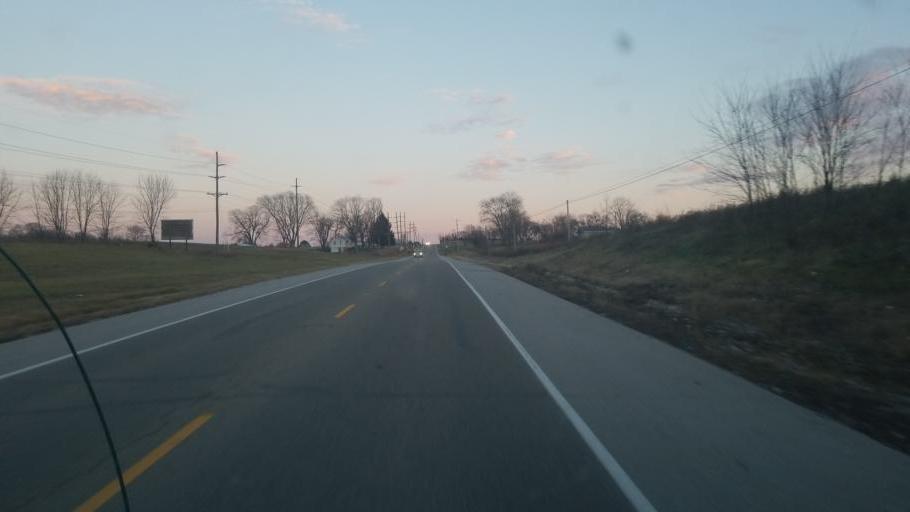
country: US
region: Indiana
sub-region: Lawrence County
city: Bedford
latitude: 38.8752
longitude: -86.3790
